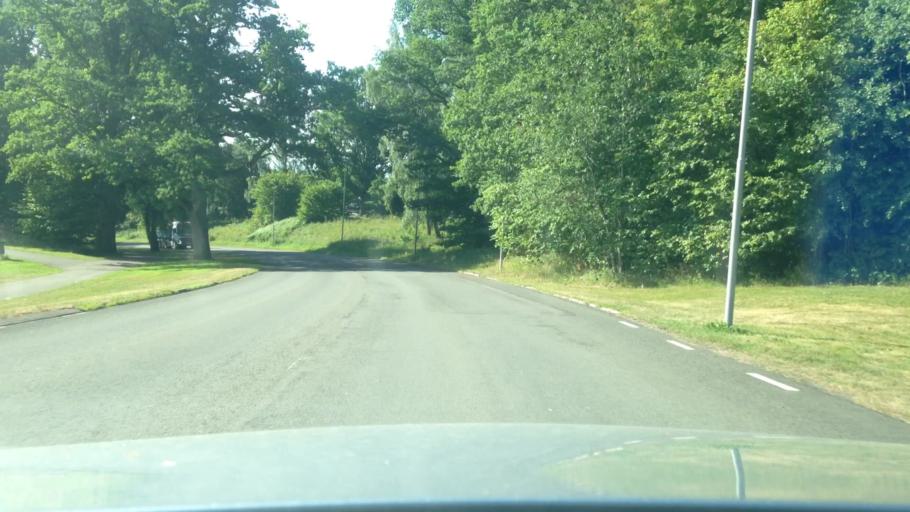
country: SE
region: Vaestra Goetaland
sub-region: Skovde Kommun
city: Skoevde
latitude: 58.3969
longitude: 13.8185
